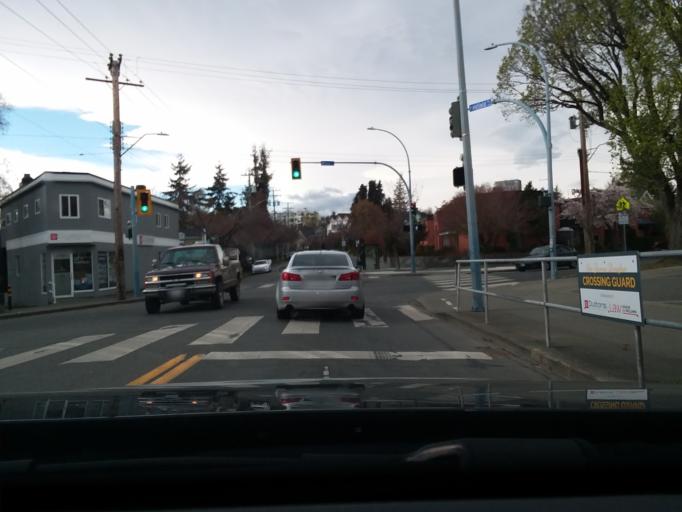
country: CA
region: British Columbia
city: Victoria
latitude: 48.4151
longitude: -123.3487
